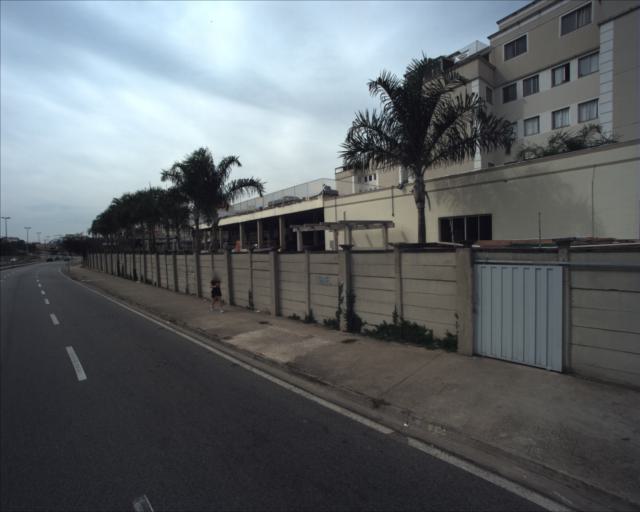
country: BR
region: Sao Paulo
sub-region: Sorocaba
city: Sorocaba
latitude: -23.4802
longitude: -47.4572
